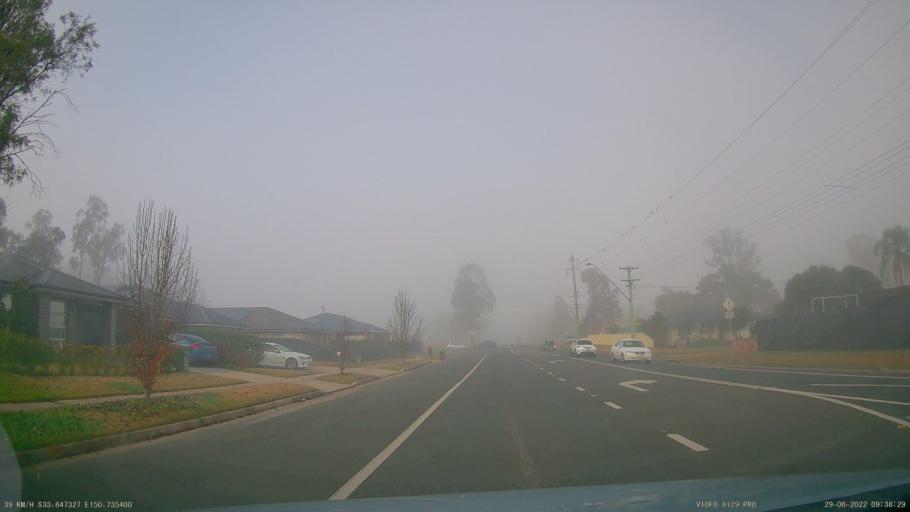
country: AU
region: New South Wales
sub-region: Hawkesbury
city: Richmond
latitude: -33.6476
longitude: 150.7353
